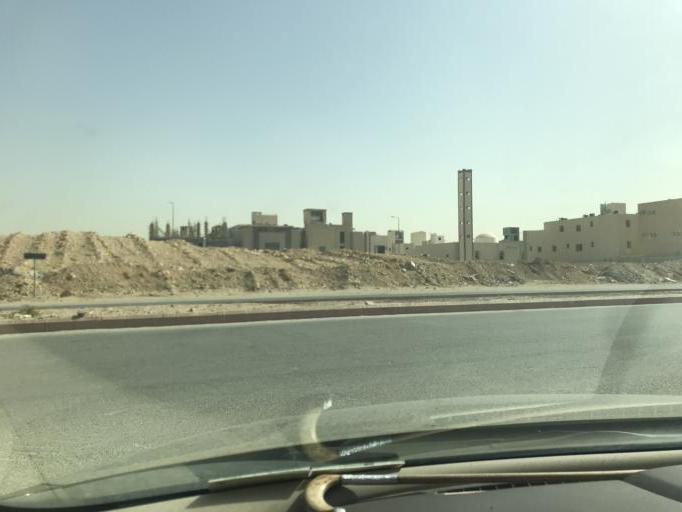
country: SA
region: Ar Riyad
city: Riyadh
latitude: 24.8253
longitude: 46.7308
